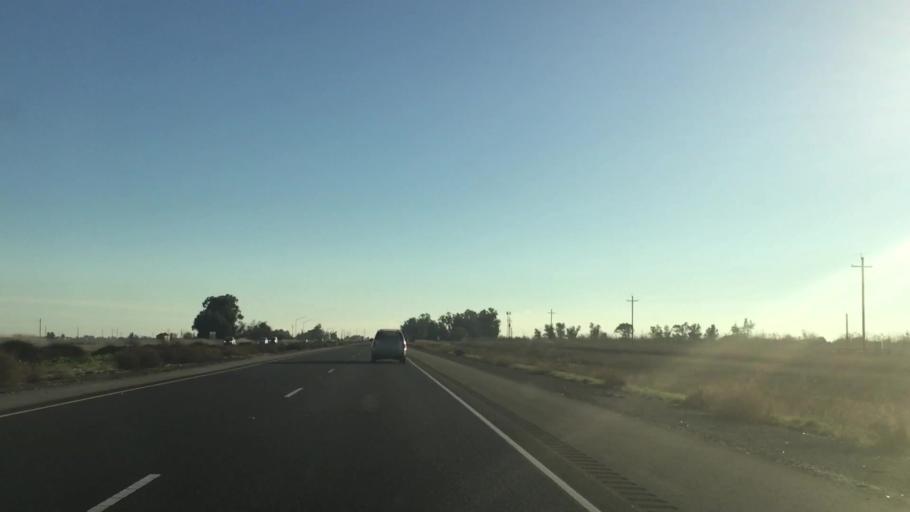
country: US
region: California
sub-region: Yuba County
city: Plumas Lake
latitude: 38.8736
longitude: -121.5436
